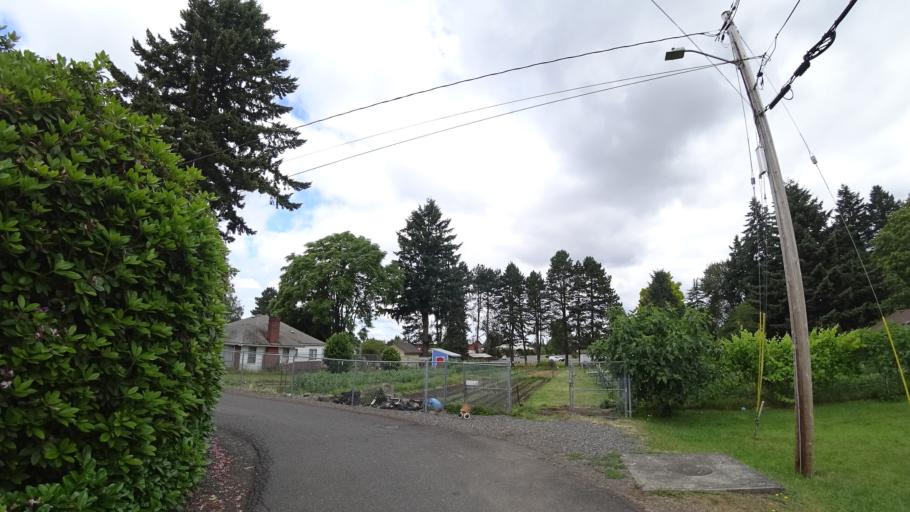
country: US
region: Oregon
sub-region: Multnomah County
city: Portland
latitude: 45.5602
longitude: -122.6058
